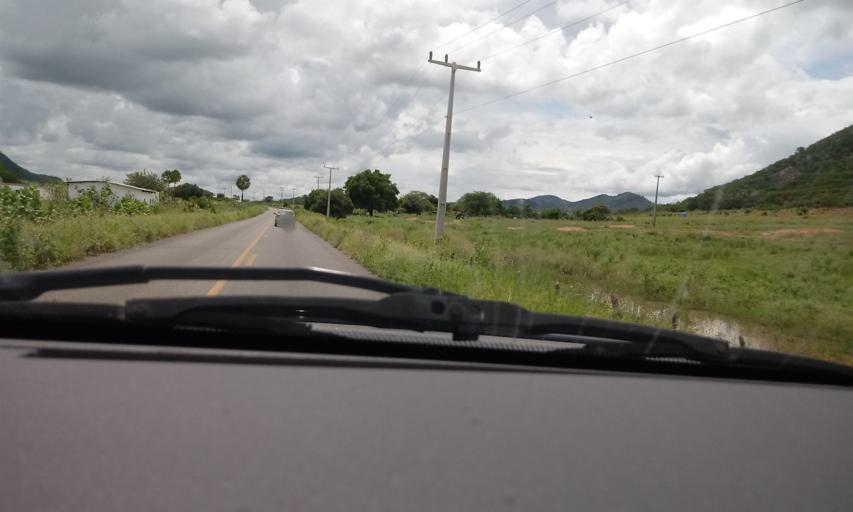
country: BR
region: Bahia
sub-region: Guanambi
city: Guanambi
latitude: -14.1384
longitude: -42.8470
